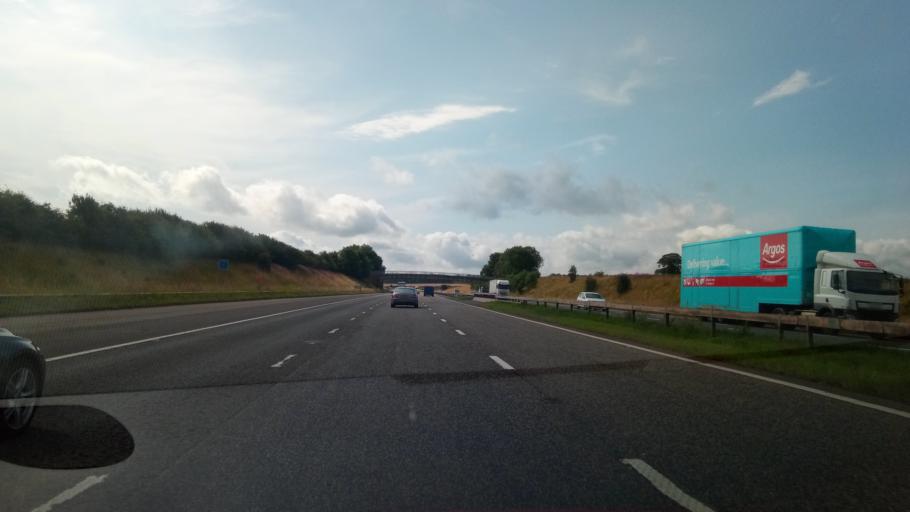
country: GB
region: England
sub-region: Cumbria
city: Penrith
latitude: 54.6253
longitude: -2.7224
